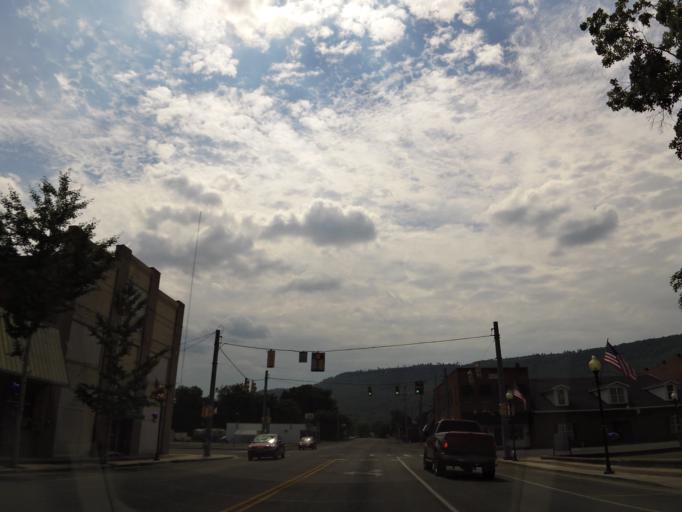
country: US
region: Tennessee
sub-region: Marion County
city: Jasper
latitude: 35.0741
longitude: -85.6252
